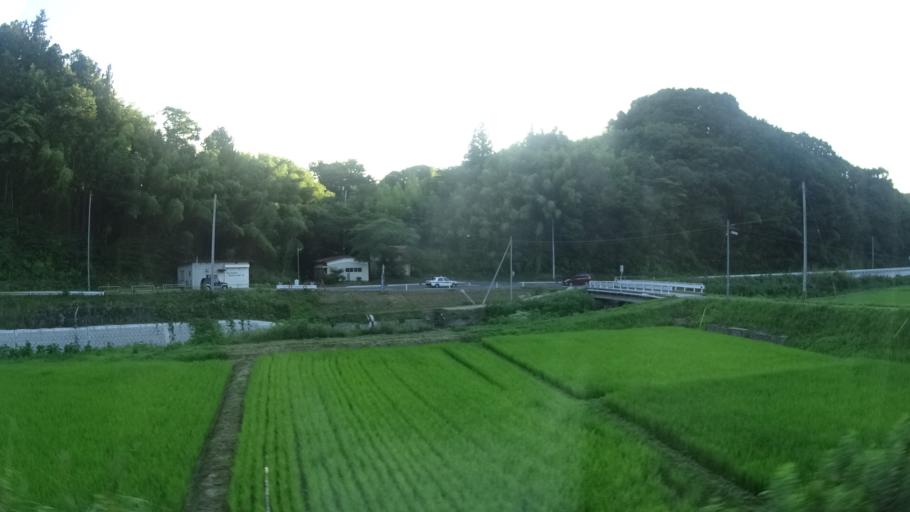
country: JP
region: Fukushima
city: Miharu
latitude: 37.4452
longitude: 140.4689
